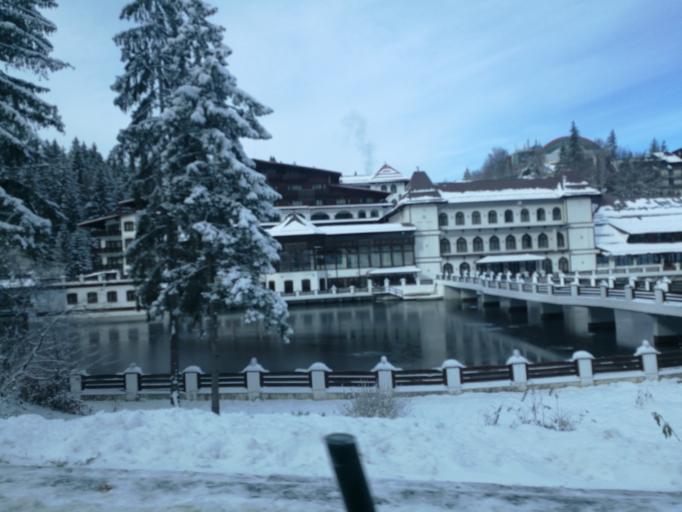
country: RO
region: Brasov
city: Brasov
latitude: 45.5923
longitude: 25.5514
